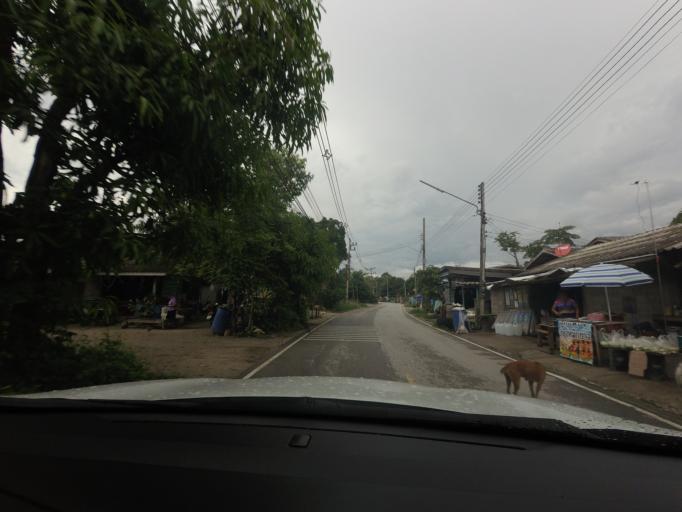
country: TH
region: Nakhon Ratchasima
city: Pak Chong
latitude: 14.6111
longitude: 101.4451
